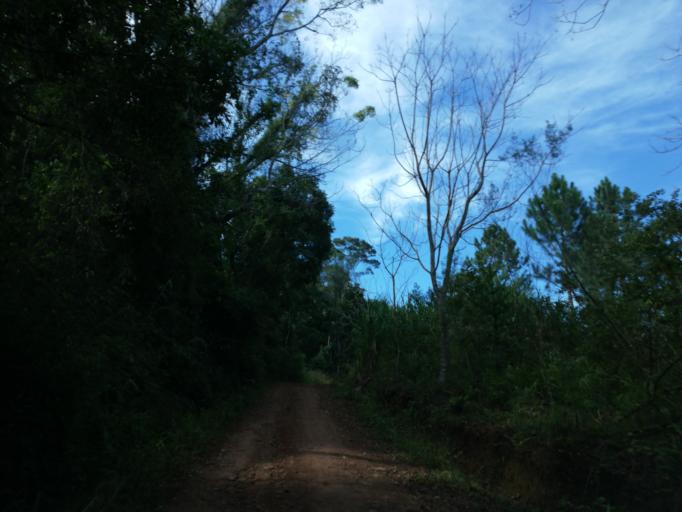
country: AR
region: Misiones
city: Dos de Mayo
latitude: -27.0151
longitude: -54.4366
